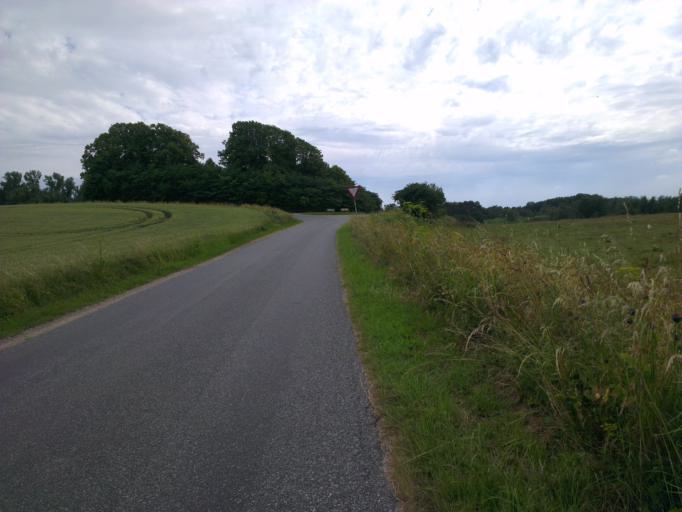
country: DK
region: Capital Region
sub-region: Frederikssund Kommune
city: Skibby
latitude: 55.7451
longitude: 12.0065
